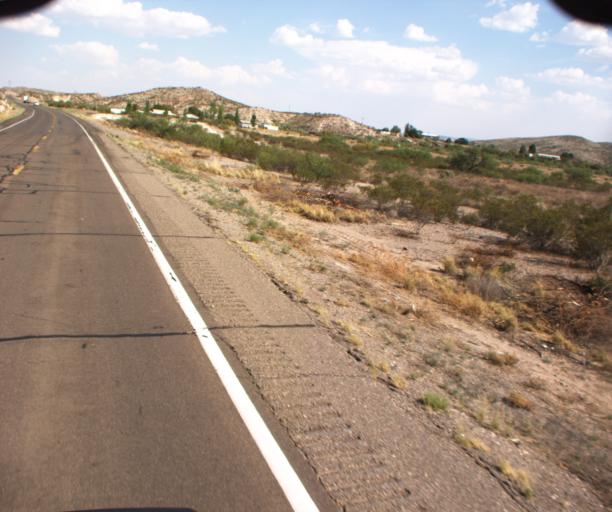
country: US
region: Arizona
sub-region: Greenlee County
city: Clifton
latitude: 32.7680
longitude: -109.1497
